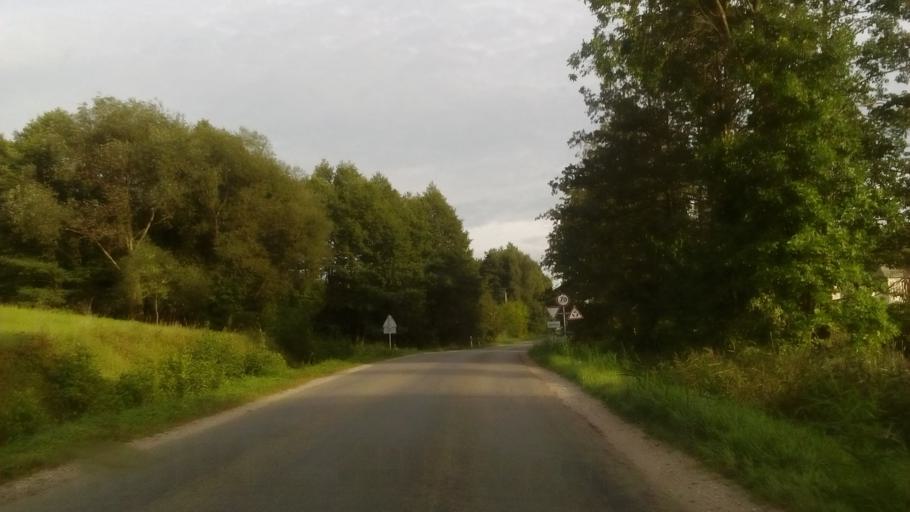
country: LT
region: Alytaus apskritis
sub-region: Alytus
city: Alytus
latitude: 54.3267
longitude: 23.9240
